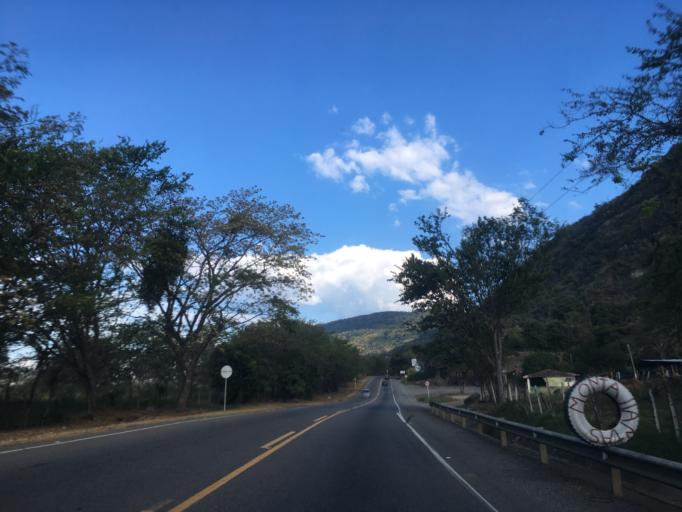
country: CO
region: Santander
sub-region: San Gil
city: San Gil
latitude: 6.5249
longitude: -73.1951
